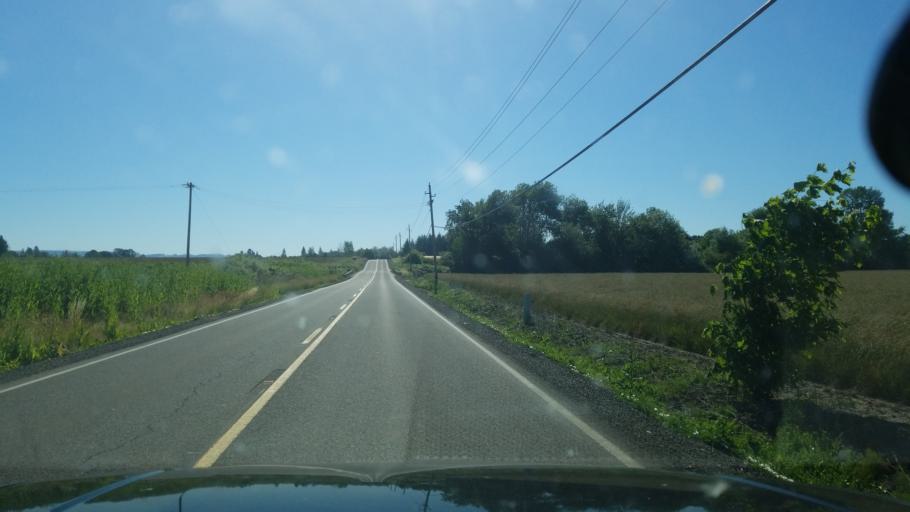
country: US
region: Oregon
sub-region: Yamhill County
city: McMinnville
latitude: 45.2305
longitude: -123.2389
